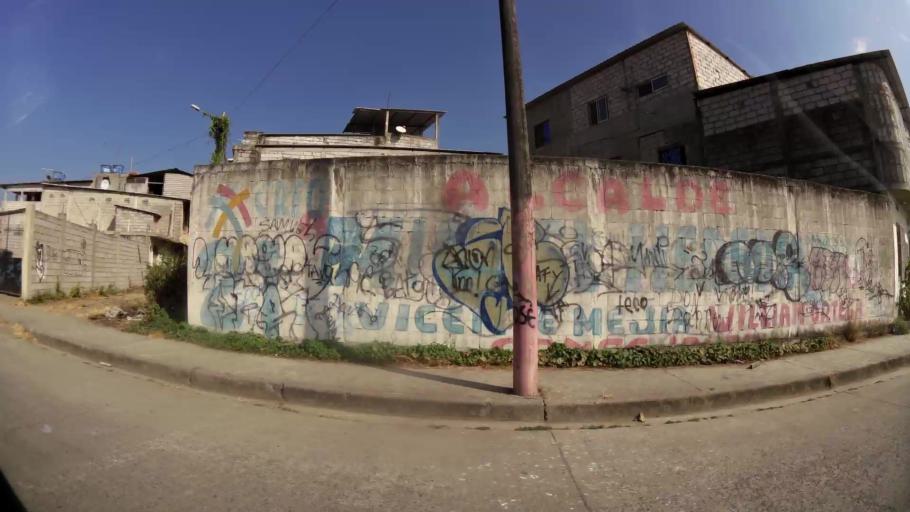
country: EC
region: Guayas
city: Eloy Alfaro
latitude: -2.1699
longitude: -79.7977
